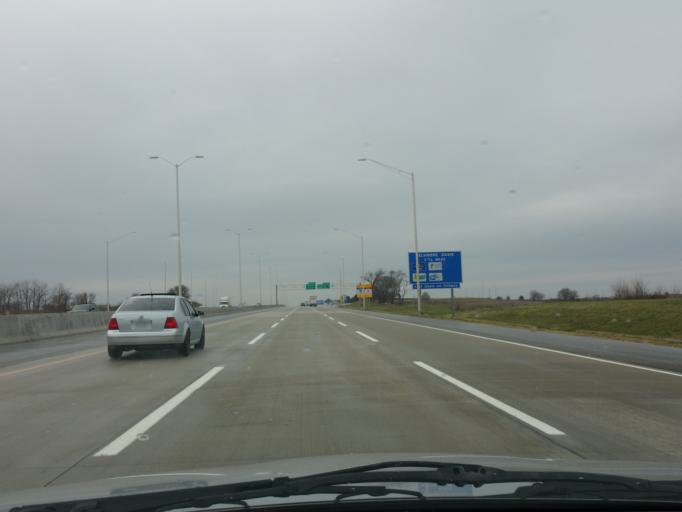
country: US
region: Illinois
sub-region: Boone County
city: Belvidere
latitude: 42.2340
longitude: -88.8041
